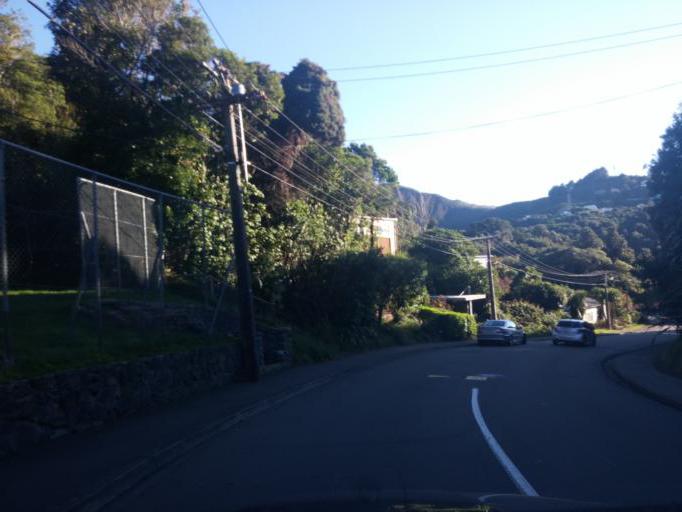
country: NZ
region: Wellington
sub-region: Wellington City
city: Kelburn
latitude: -41.2688
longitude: 174.7598
